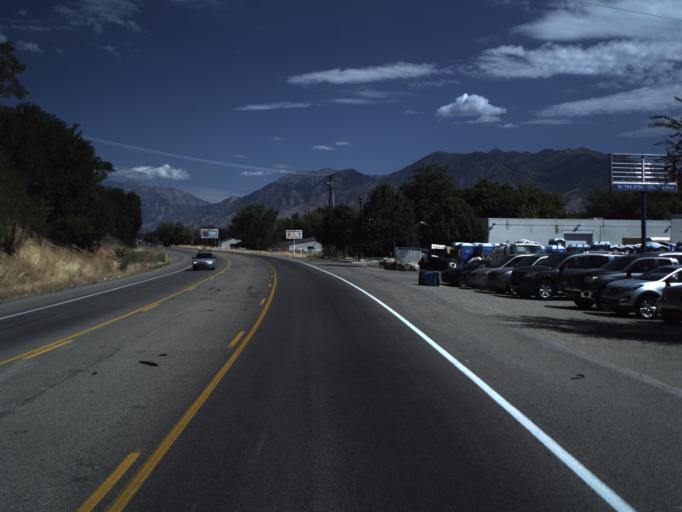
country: US
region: Utah
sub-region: Utah County
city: Spanish Fork
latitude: 40.0869
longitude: -111.6562
